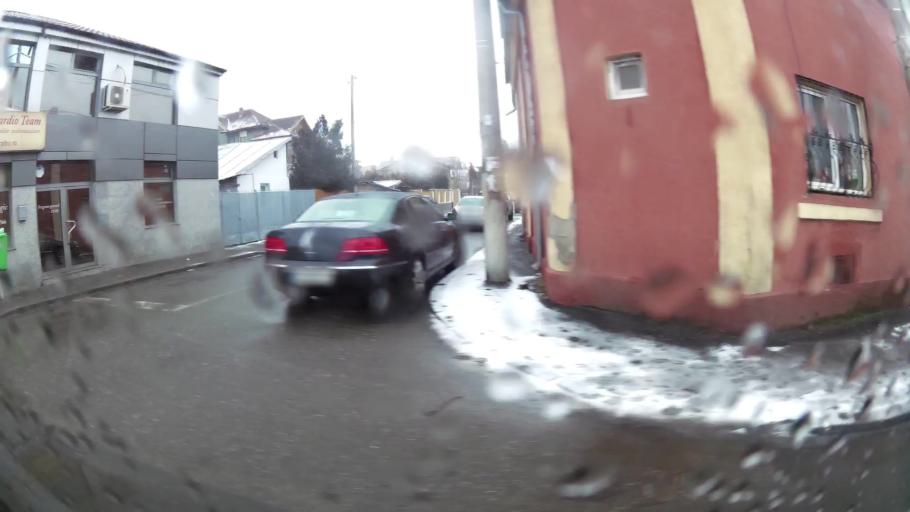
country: RO
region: Prahova
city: Ploiesti
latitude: 44.9463
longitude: 26.0074
